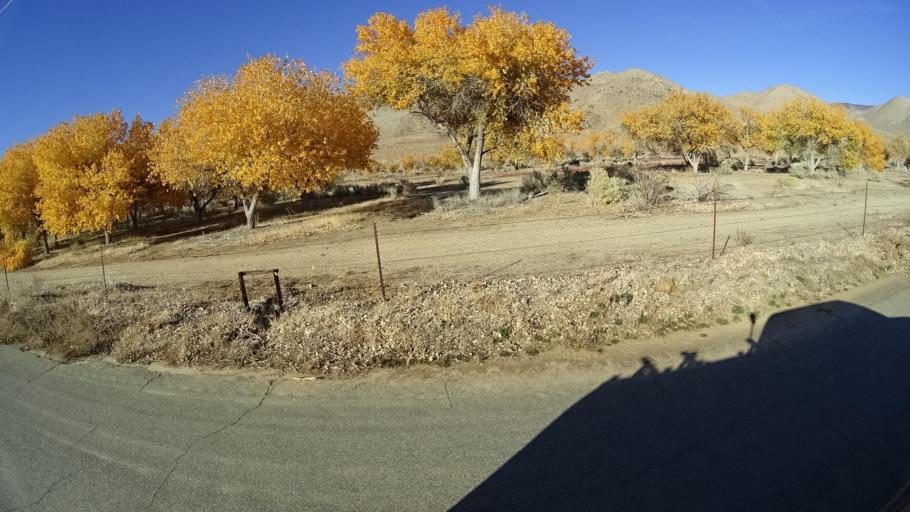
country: US
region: California
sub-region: Kern County
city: Weldon
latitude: 35.5576
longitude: -118.2320
